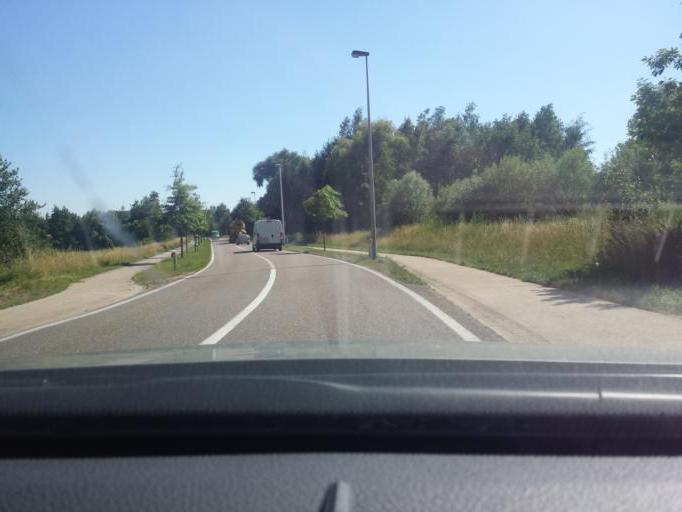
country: BE
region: Flanders
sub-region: Provincie Limburg
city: Lummen
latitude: 50.9678
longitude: 5.1846
